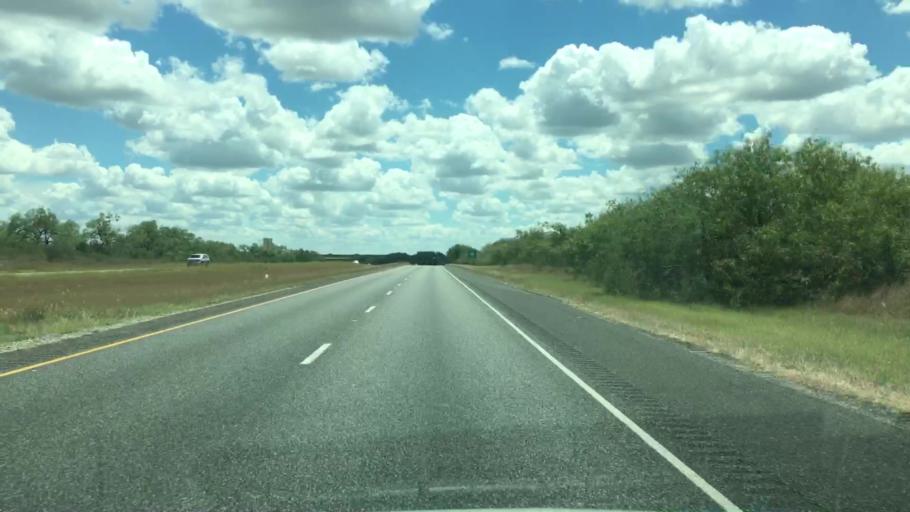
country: US
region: Texas
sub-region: Atascosa County
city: Pleasanton
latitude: 28.9158
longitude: -98.4349
